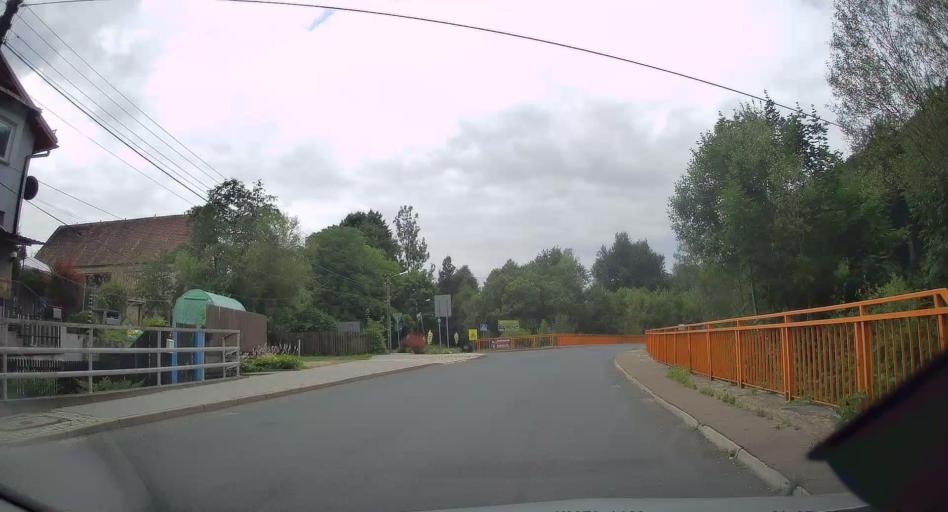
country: PL
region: Lower Silesian Voivodeship
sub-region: Powiat walbrzyski
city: Gluszyca
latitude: 50.7291
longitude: 16.4011
